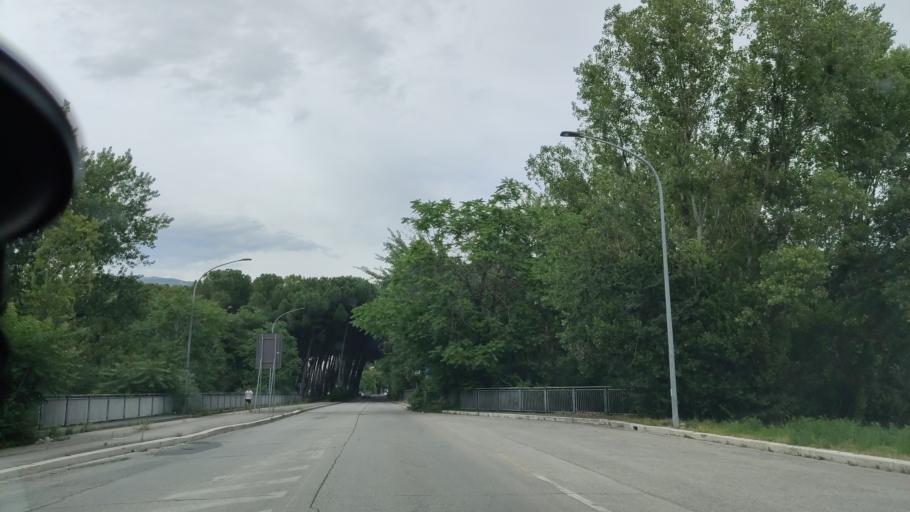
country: IT
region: Umbria
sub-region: Provincia di Terni
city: Terni
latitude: 42.5606
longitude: 12.6576
